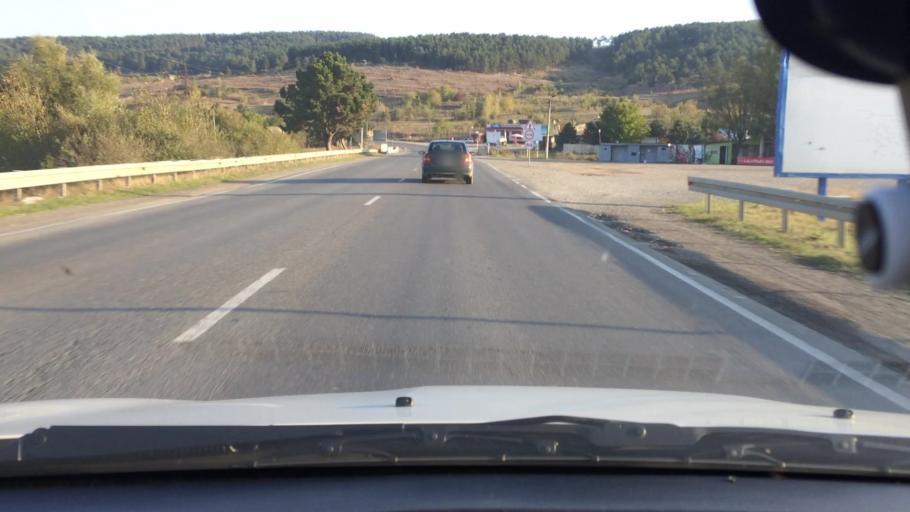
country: GE
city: Surami
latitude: 42.0092
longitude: 43.5774
